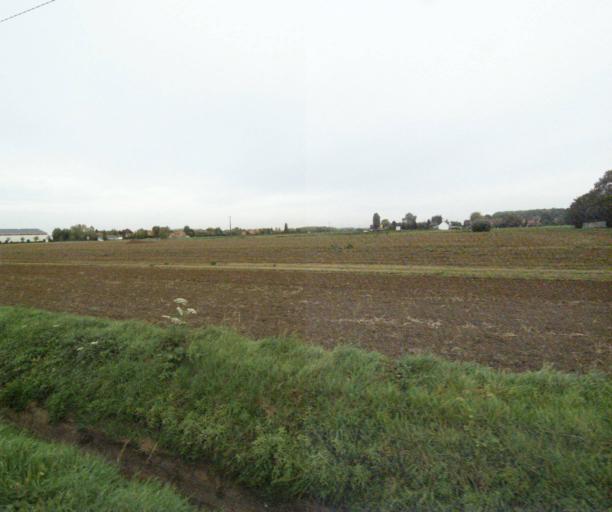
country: FR
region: Nord-Pas-de-Calais
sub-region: Departement du Nord
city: Aubers
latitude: 50.5924
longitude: 2.8318
